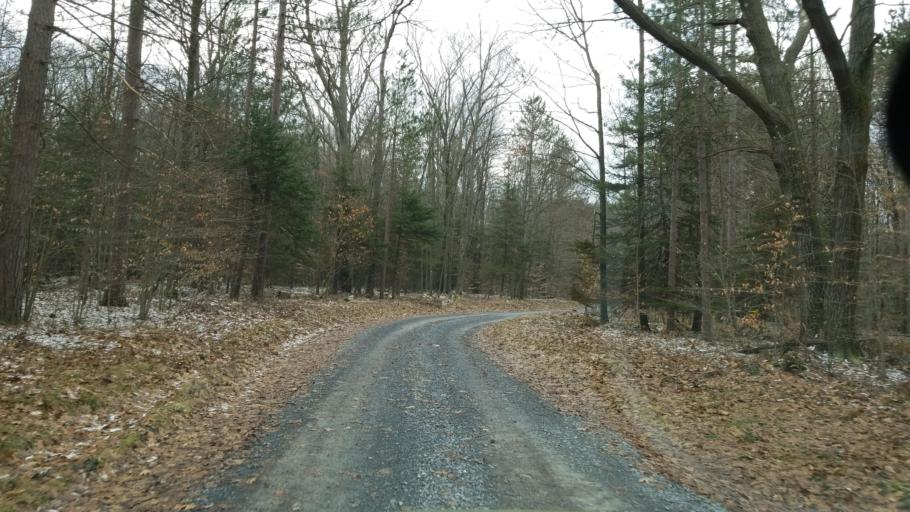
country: US
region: Pennsylvania
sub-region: Clearfield County
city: Clearfield
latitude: 41.1406
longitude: -78.5378
